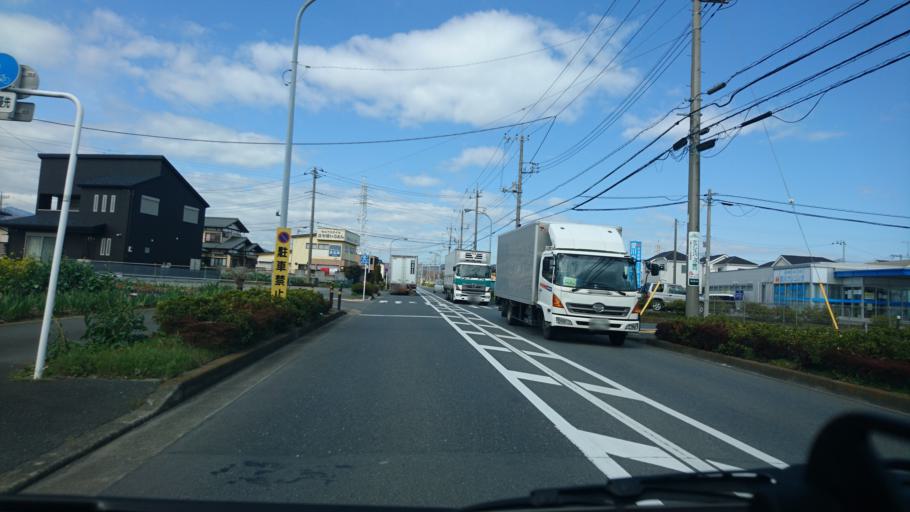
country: JP
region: Kanagawa
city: Zama
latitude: 35.5263
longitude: 139.3425
